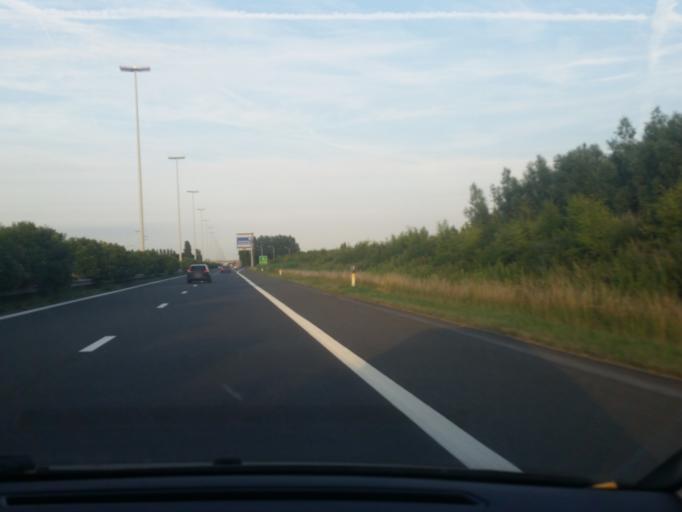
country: BE
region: Flanders
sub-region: Provincie West-Vlaanderen
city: Bredene
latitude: 51.2062
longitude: 2.9682
